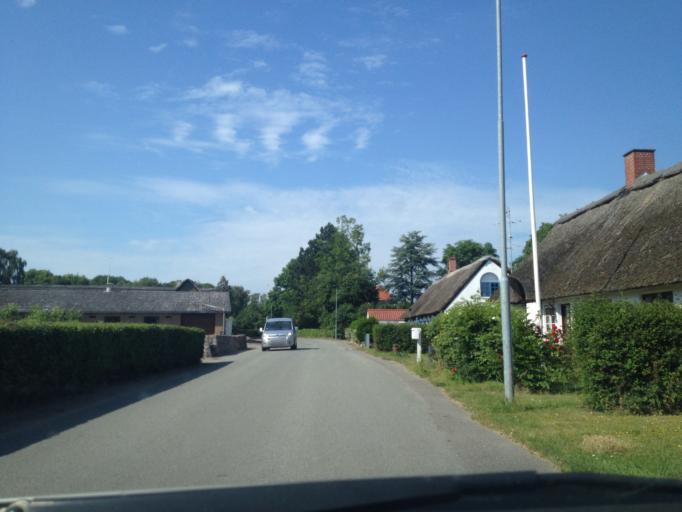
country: DK
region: Central Jutland
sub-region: Samso Kommune
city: Tranebjerg
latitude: 55.8106
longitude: 10.5561
